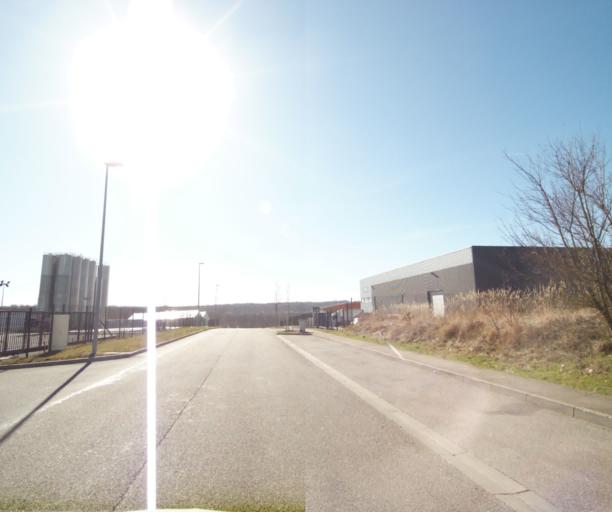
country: FR
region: Lorraine
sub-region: Departement de Meurthe-et-Moselle
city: Richardmenil
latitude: 48.6118
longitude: 6.1818
